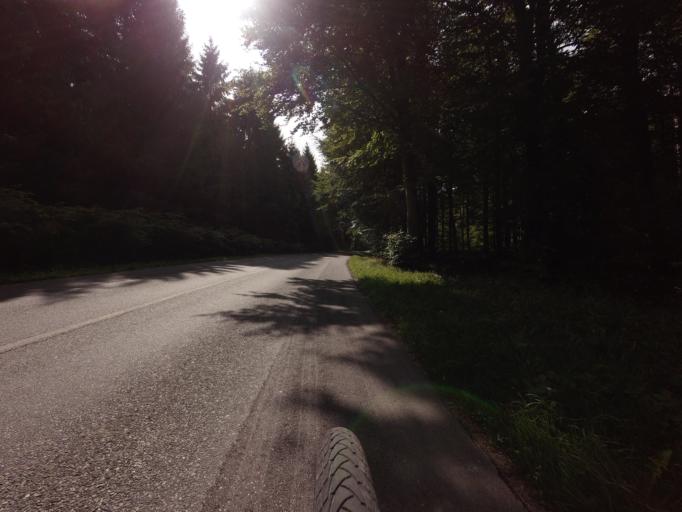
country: DK
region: Zealand
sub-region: Faxe Kommune
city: Fakse Ladeplads
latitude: 55.2365
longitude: 12.2131
